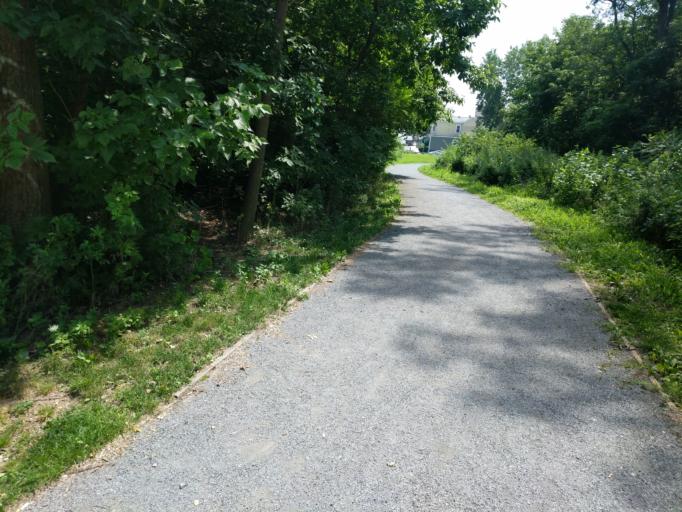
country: US
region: New York
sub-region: Bronx
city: The Bronx
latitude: 40.7888
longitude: -73.8374
